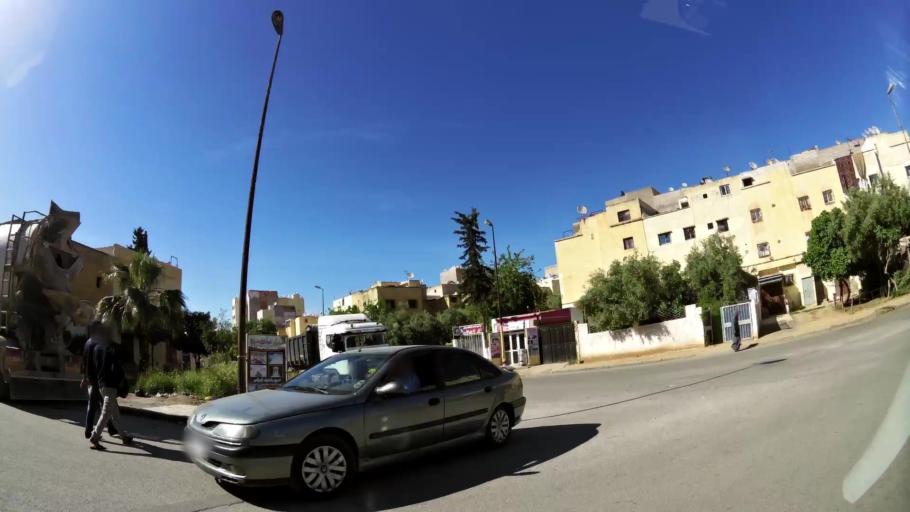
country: MA
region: Fes-Boulemane
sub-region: Fes
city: Fes
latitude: 34.0170
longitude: -4.9718
